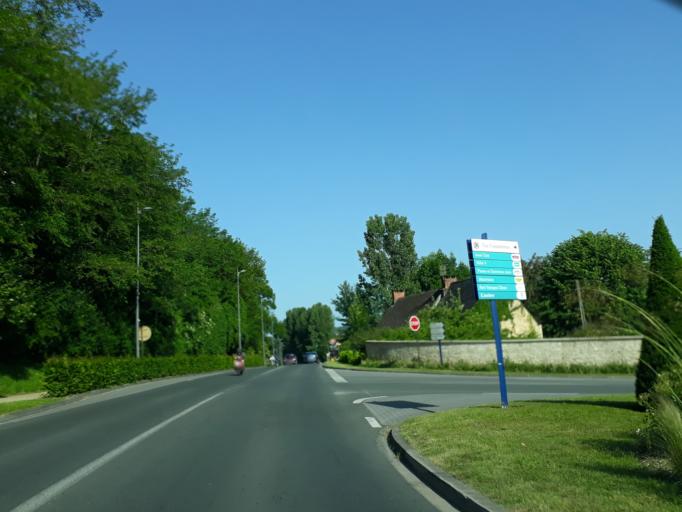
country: FR
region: Aquitaine
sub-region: Departement de la Dordogne
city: Terrasson-Lavilledieu
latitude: 45.1287
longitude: 1.3152
